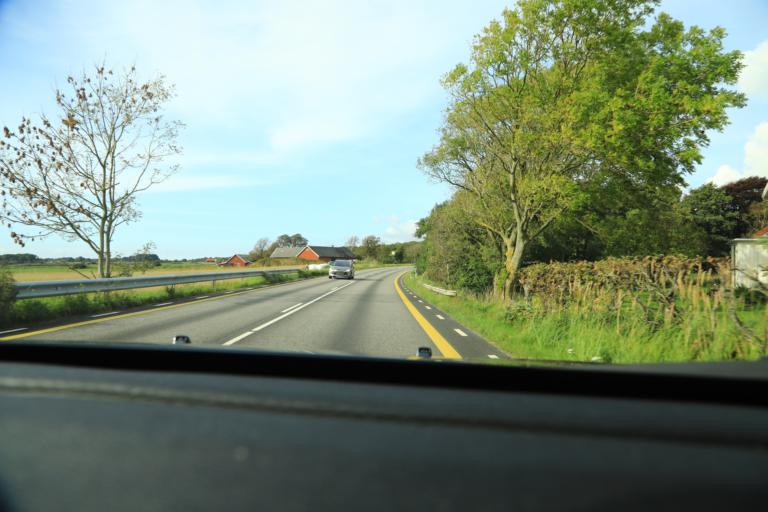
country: SE
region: Halland
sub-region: Varbergs Kommun
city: Traslovslage
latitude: 57.0368
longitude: 12.3254
